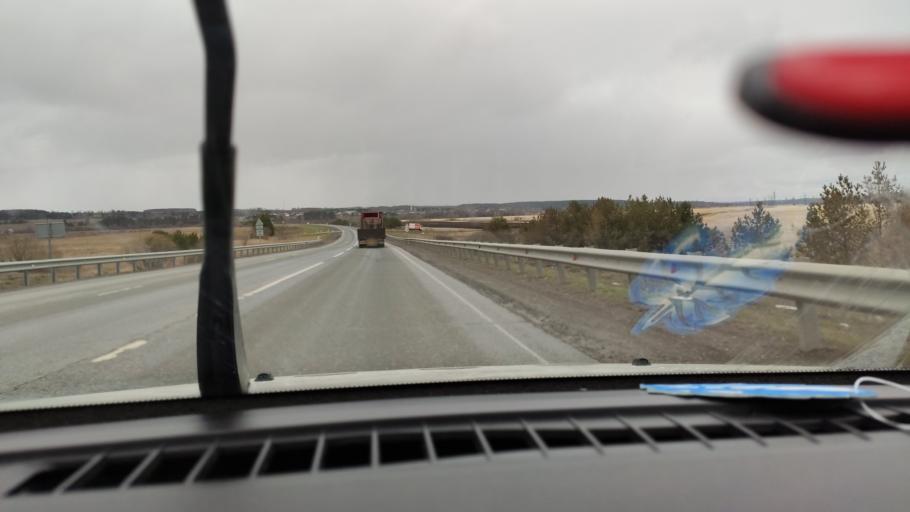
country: RU
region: Perm
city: Kungur
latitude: 57.3588
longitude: 56.9308
